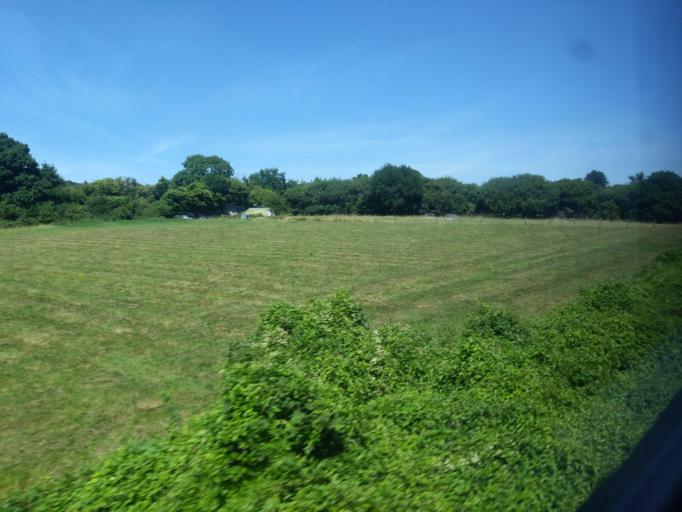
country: GB
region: England
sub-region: Devon
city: South Brent
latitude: 50.4286
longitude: -3.8244
